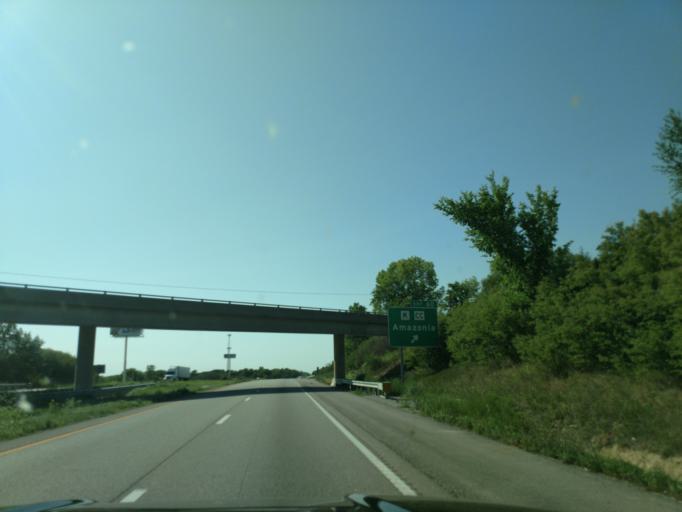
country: US
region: Missouri
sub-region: Andrew County
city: Savannah
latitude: 39.9158
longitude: -94.9041
